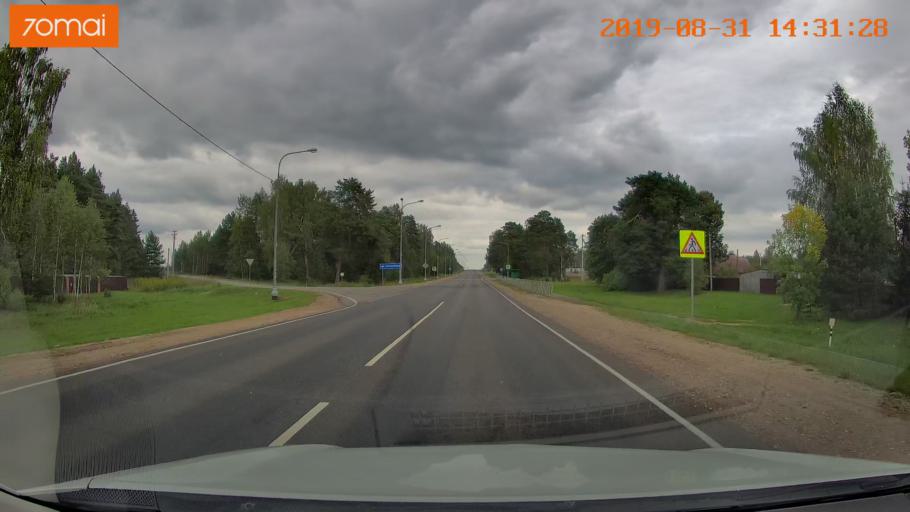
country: RU
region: Smolensk
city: Yekimovichi
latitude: 54.1382
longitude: 33.3731
